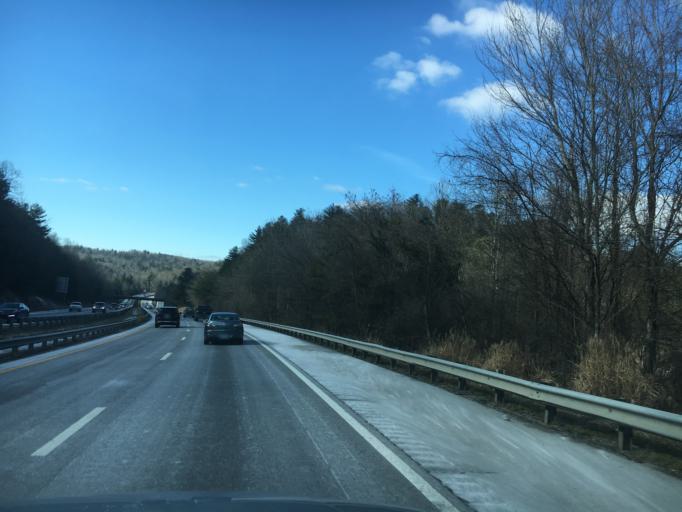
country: US
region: North Carolina
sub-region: Henderson County
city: Dana
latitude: 35.2531
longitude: -82.3435
